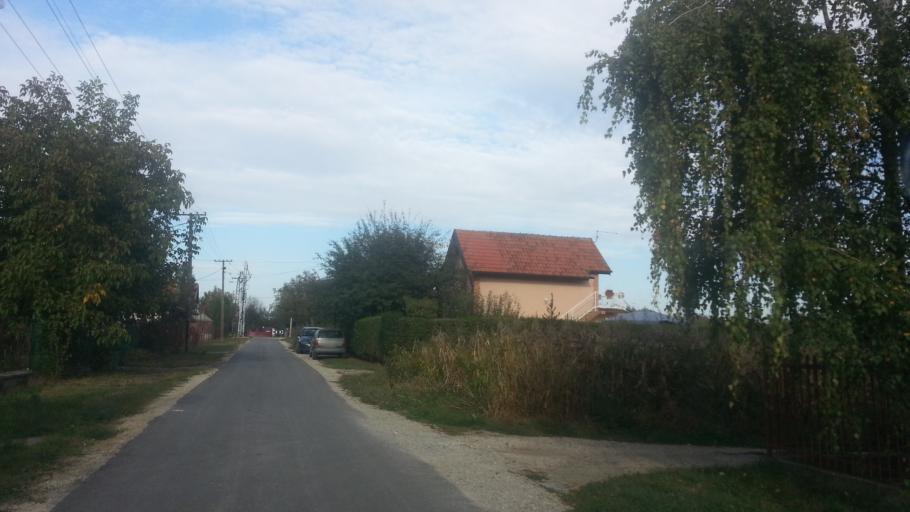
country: RS
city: Belegis
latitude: 45.0235
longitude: 20.3473
